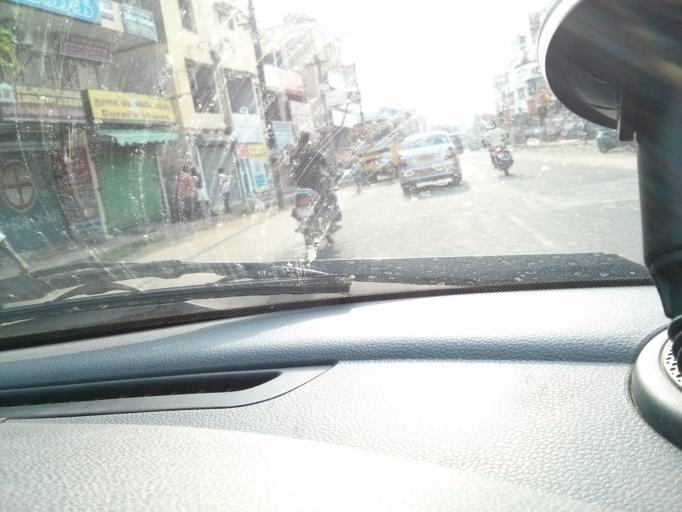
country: IN
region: Tamil Nadu
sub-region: Coimbatore
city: Coimbatore
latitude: 11.0263
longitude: 76.9443
